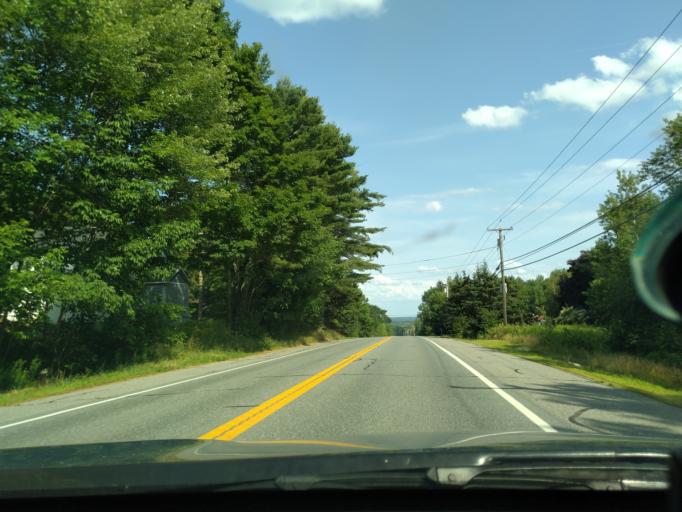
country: US
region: Maine
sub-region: Hancock County
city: Surry
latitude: 44.5435
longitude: -68.5119
